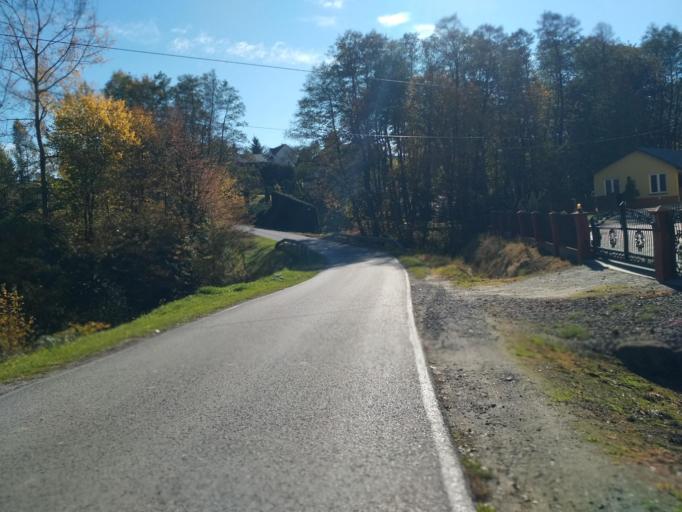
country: PL
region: Subcarpathian Voivodeship
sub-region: Powiat ropczycko-sedziszowski
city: Iwierzyce
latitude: 49.9818
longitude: 21.7261
